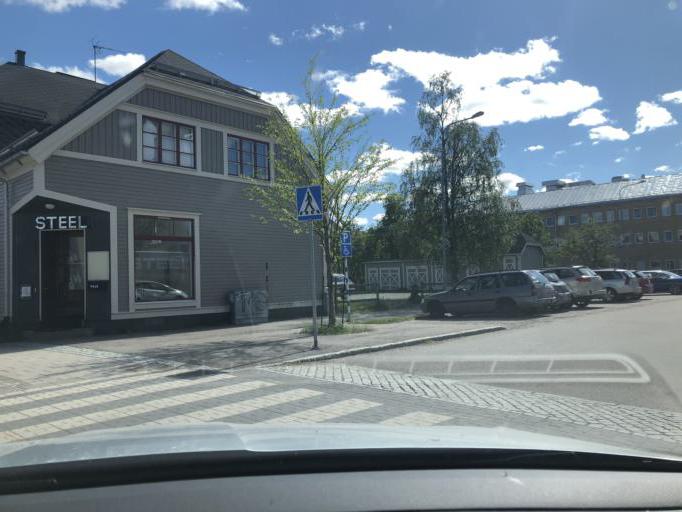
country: SE
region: Norrbotten
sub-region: Gallivare Kommun
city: Gaellivare
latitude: 67.1350
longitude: 20.6583
